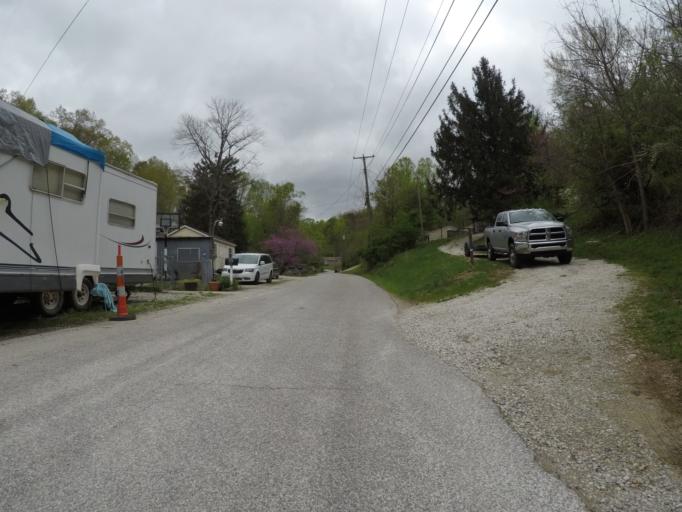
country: US
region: West Virginia
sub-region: Cabell County
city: Barboursville
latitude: 38.4062
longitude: -82.2836
